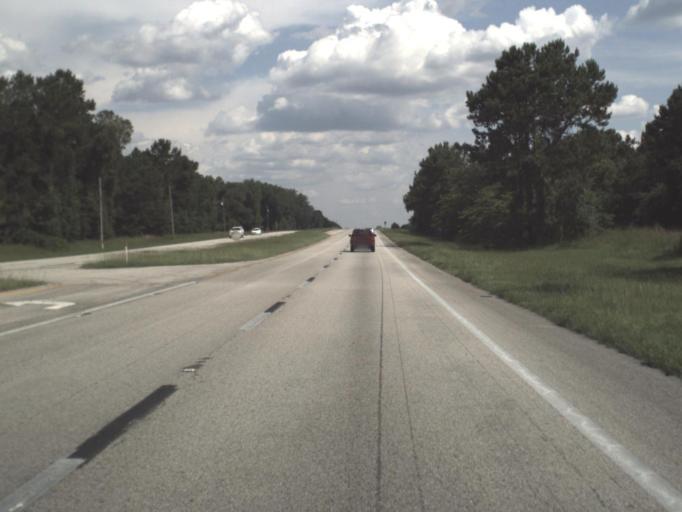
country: US
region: Florida
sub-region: Alachua County
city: Hawthorne
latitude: 29.6334
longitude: -82.1031
